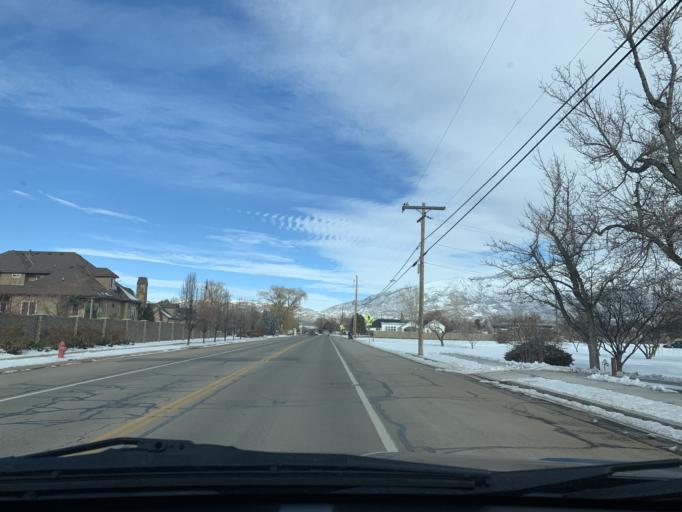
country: US
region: Utah
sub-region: Utah County
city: Lehi
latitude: 40.4122
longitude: -111.8208
